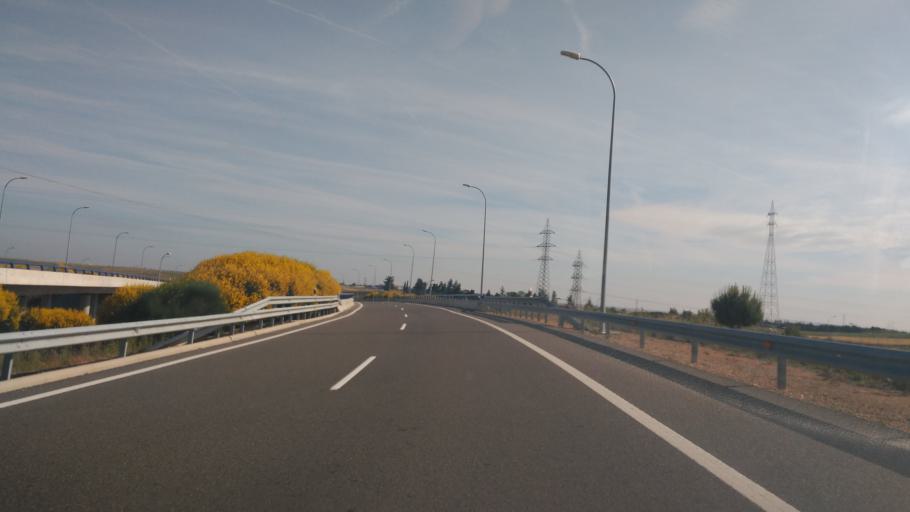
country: ES
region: Castille and Leon
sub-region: Provincia de Salamanca
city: Villamayor
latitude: 40.9951
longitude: -5.6744
